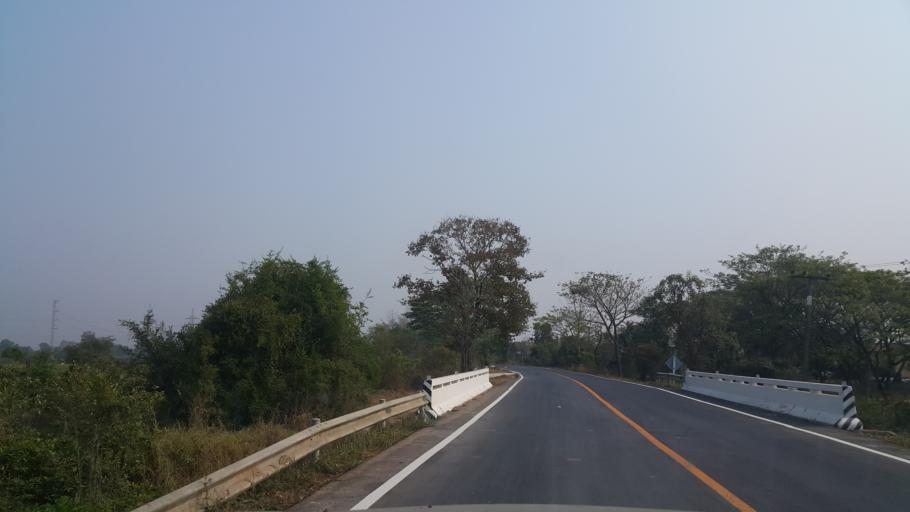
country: TH
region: Lamphun
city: Ban Thi
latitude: 18.6727
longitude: 99.0798
